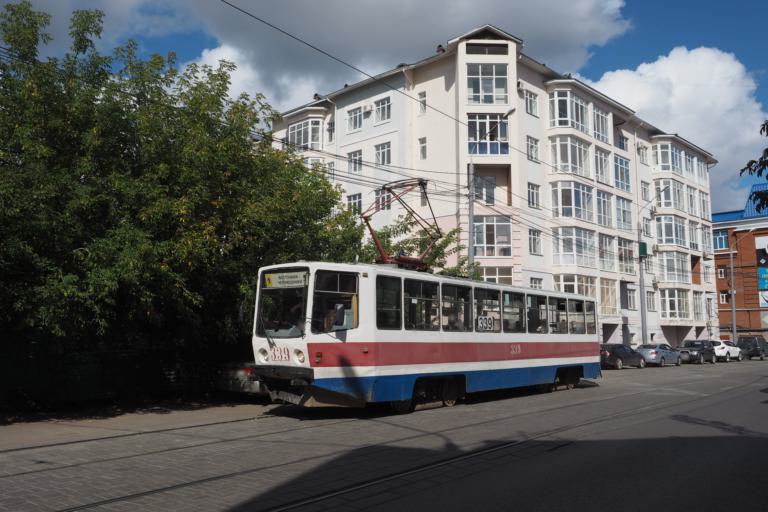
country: RU
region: Tomsk
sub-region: Tomskiy Rayon
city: Tomsk
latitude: 56.4854
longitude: 84.9518
